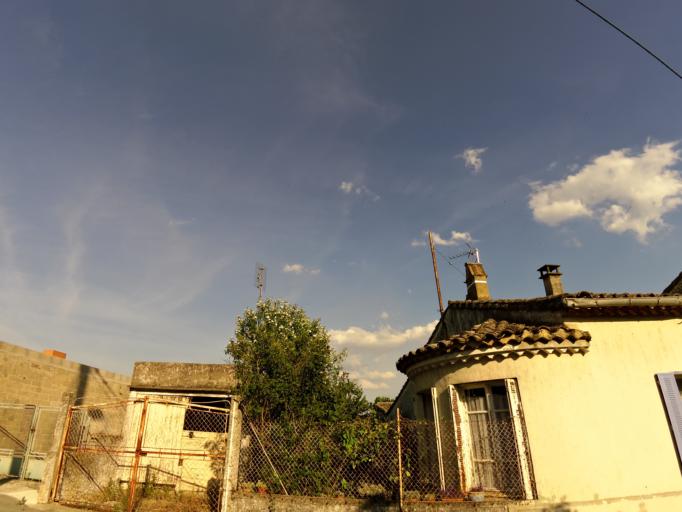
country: FR
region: Languedoc-Roussillon
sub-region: Departement du Gard
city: Quissac
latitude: 43.8740
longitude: 4.0422
